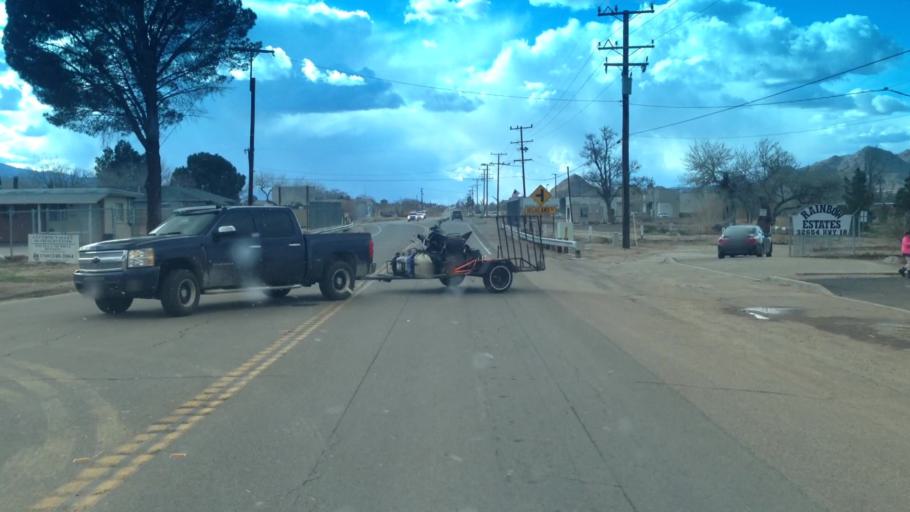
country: US
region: California
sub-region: San Bernardino County
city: Lucerne Valley
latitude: 34.4439
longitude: -116.9510
